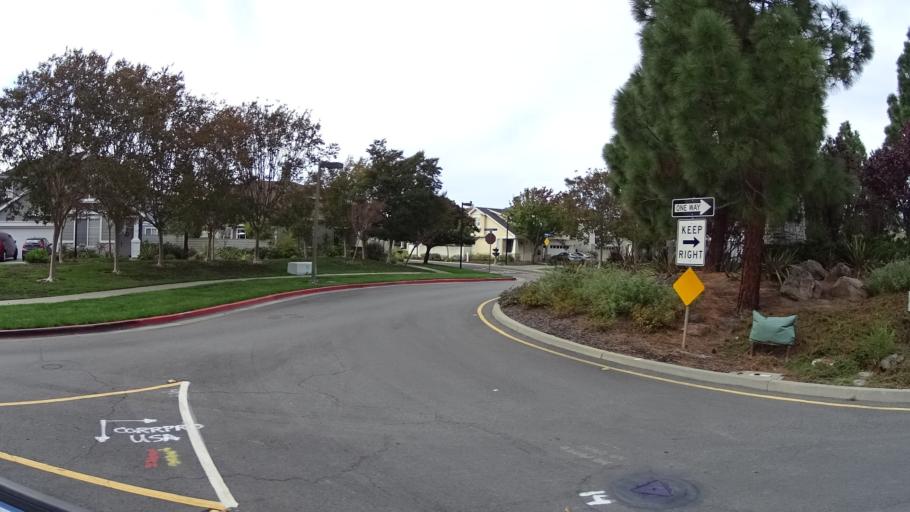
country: US
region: California
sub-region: San Mateo County
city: Redwood Shores
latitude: 37.5466
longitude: -122.2399
